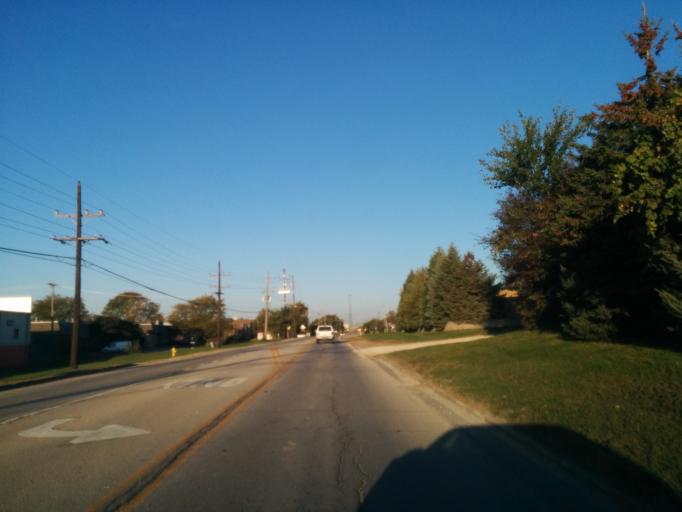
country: US
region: Illinois
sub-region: DuPage County
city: Carol Stream
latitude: 41.8978
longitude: -88.1069
